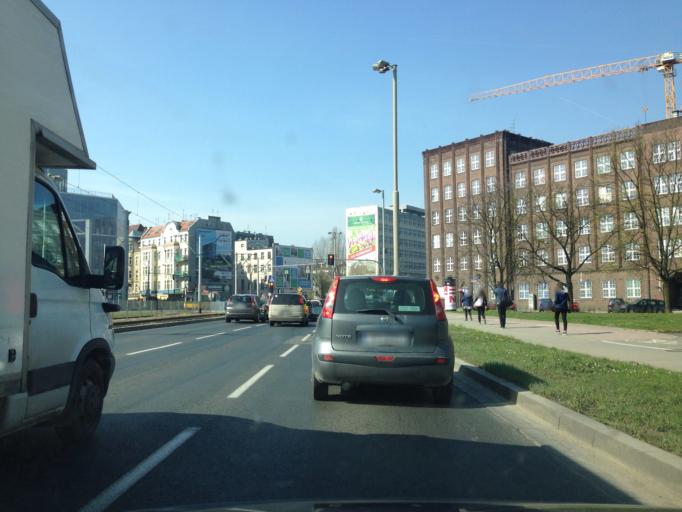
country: PL
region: Lower Silesian Voivodeship
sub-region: Powiat wroclawski
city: Wroclaw
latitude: 51.1077
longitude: 17.0453
